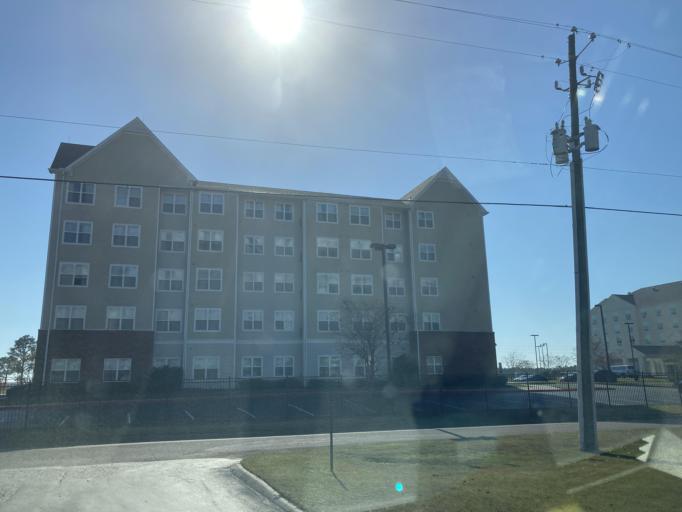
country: US
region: Mississippi
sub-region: Harrison County
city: West Gulfport
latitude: 30.4167
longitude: -89.0753
